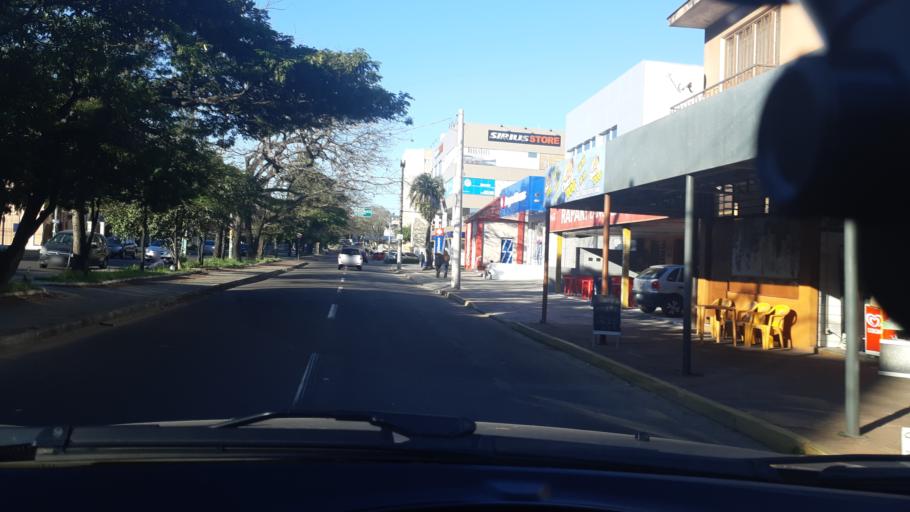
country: BR
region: Rio Grande do Sul
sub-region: Sao Leopoldo
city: Sao Leopoldo
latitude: -29.7702
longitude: -51.1413
